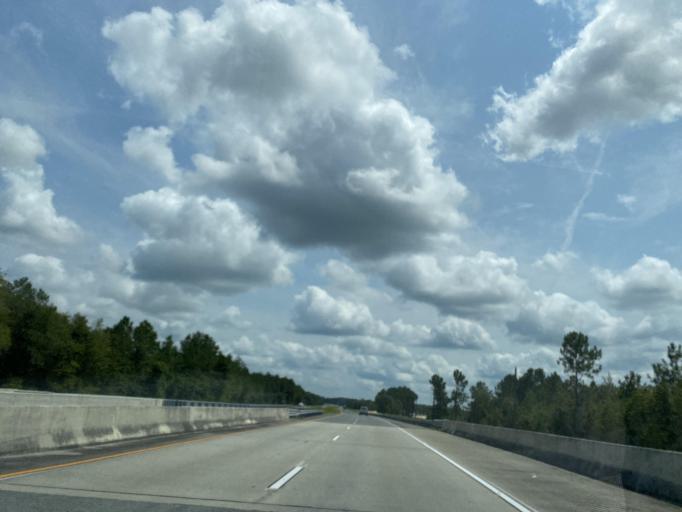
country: US
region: Georgia
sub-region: Ware County
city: Deenwood
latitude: 31.3114
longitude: -82.4563
